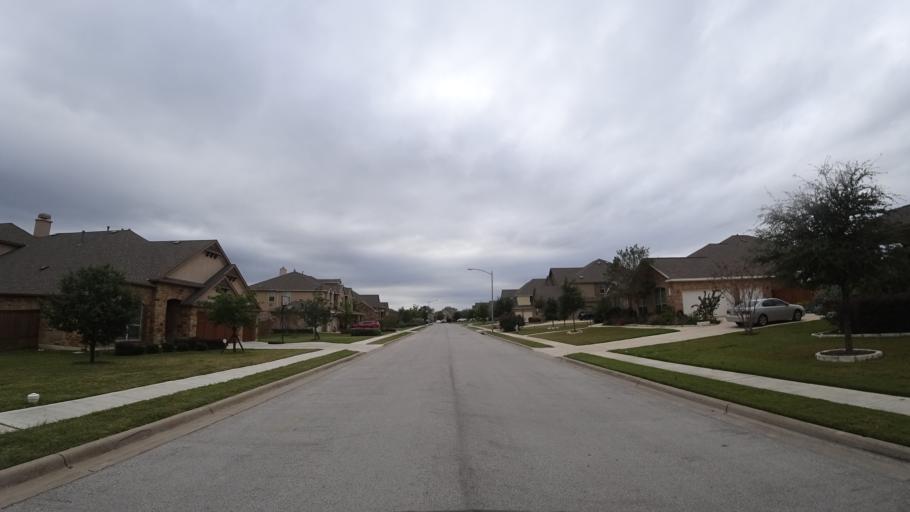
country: US
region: Texas
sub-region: Travis County
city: Shady Hollow
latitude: 30.1472
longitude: -97.8563
